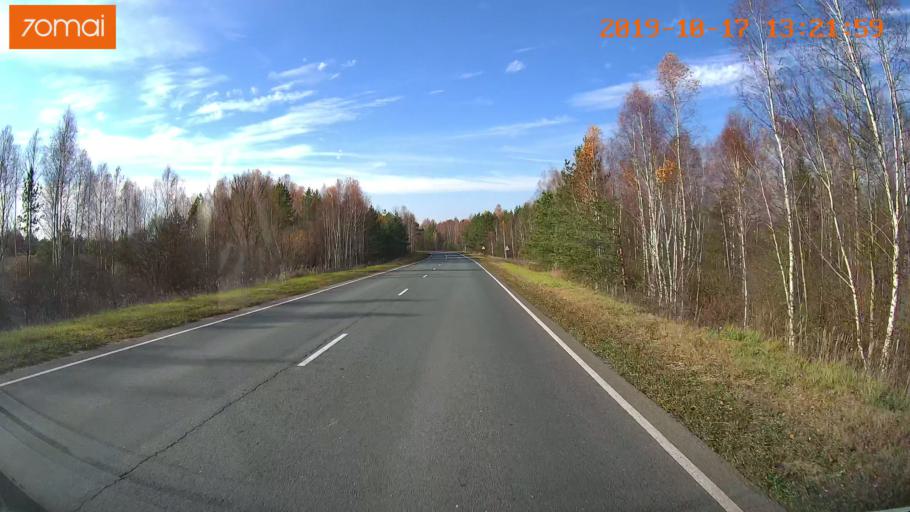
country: RU
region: Rjazan
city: Gus'-Zheleznyy
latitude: 55.0839
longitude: 41.0144
